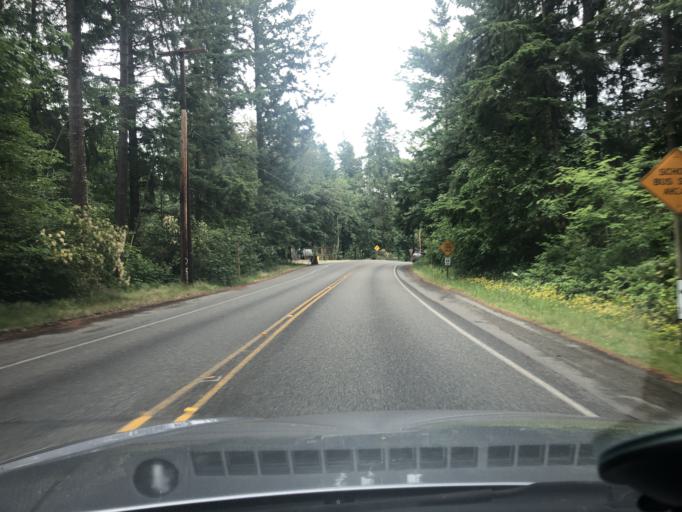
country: US
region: Washington
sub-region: King County
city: Black Diamond
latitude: 47.3366
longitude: -122.0476
